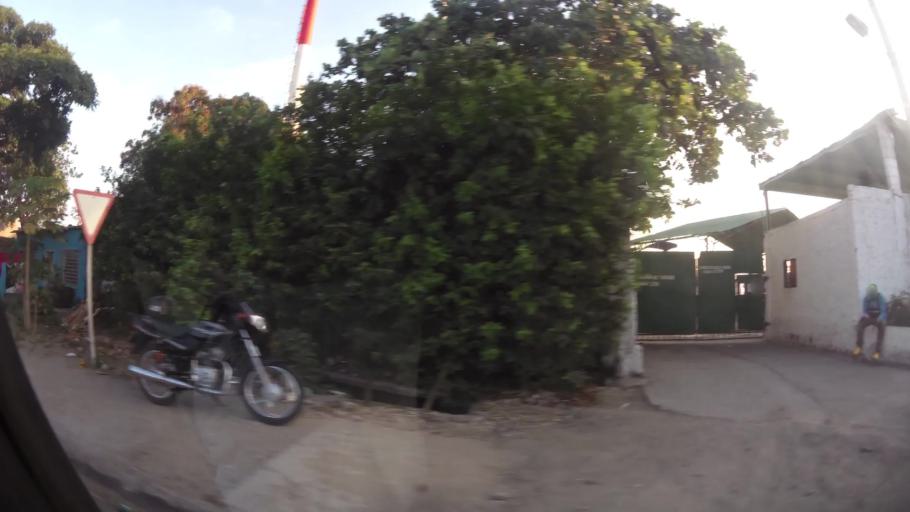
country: CO
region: Bolivar
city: Cartagena
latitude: 10.4049
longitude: -75.5233
